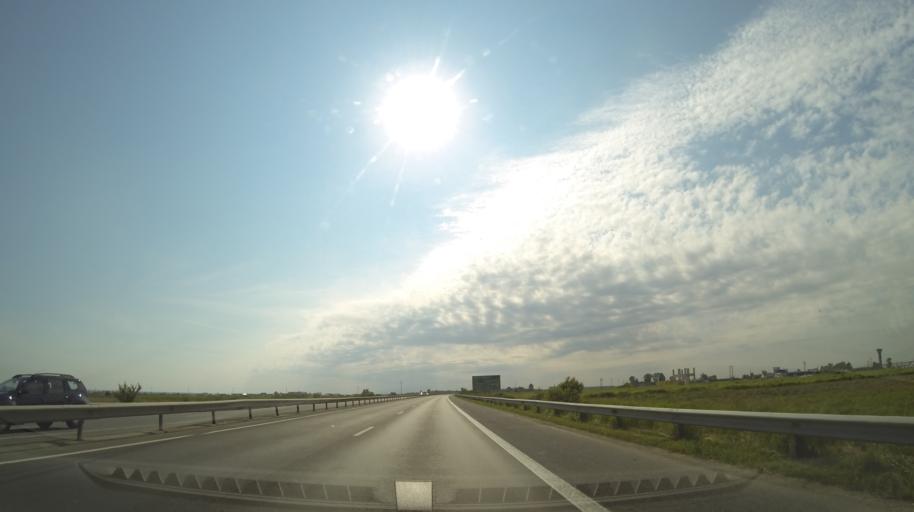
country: RO
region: Arges
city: Popesti
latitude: 44.7579
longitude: 25.0721
